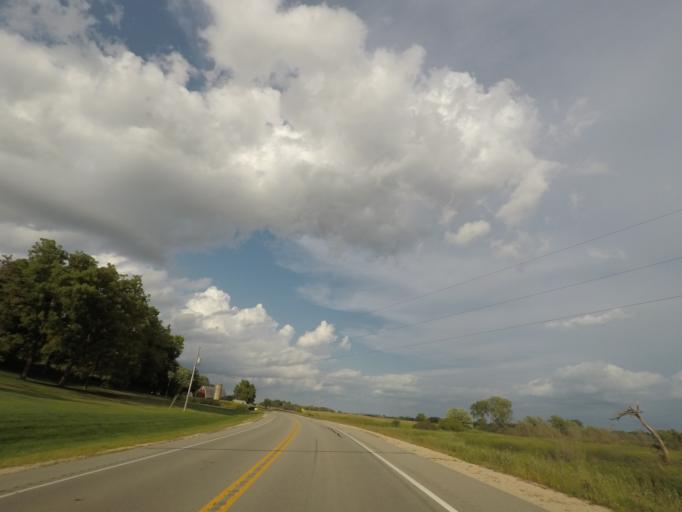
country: US
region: Wisconsin
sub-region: Dane County
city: Waunakee
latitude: 43.1895
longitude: -89.4848
